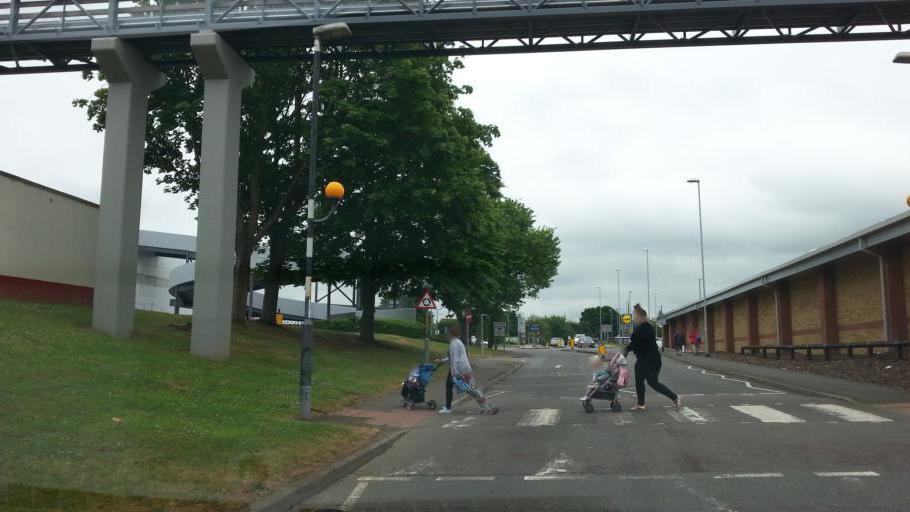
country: GB
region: England
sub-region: Northamptonshire
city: Northampton
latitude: 52.2560
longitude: -0.8360
